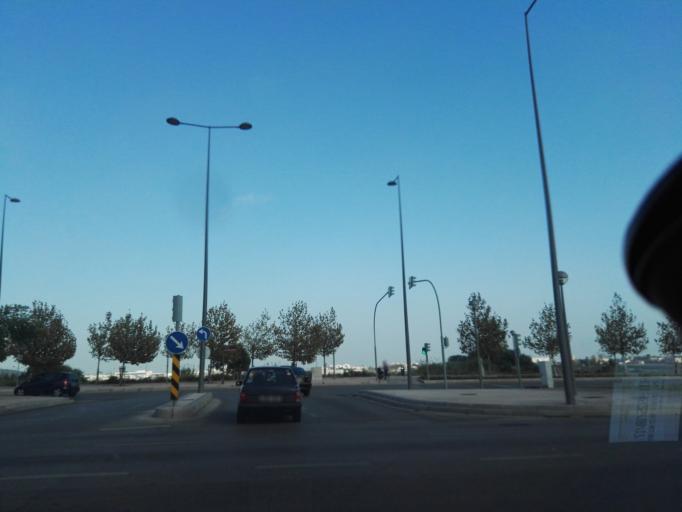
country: PT
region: Lisbon
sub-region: Odivelas
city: Olival do Basto
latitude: 38.7673
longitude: -9.1489
